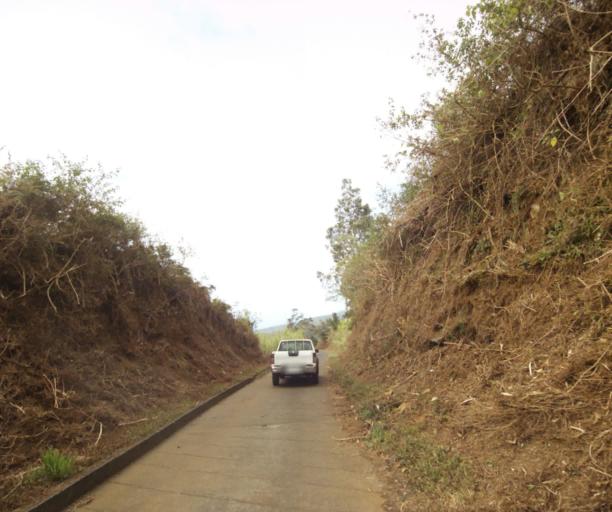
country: RE
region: Reunion
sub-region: Reunion
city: Saint-Paul
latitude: -21.0072
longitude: 55.3489
